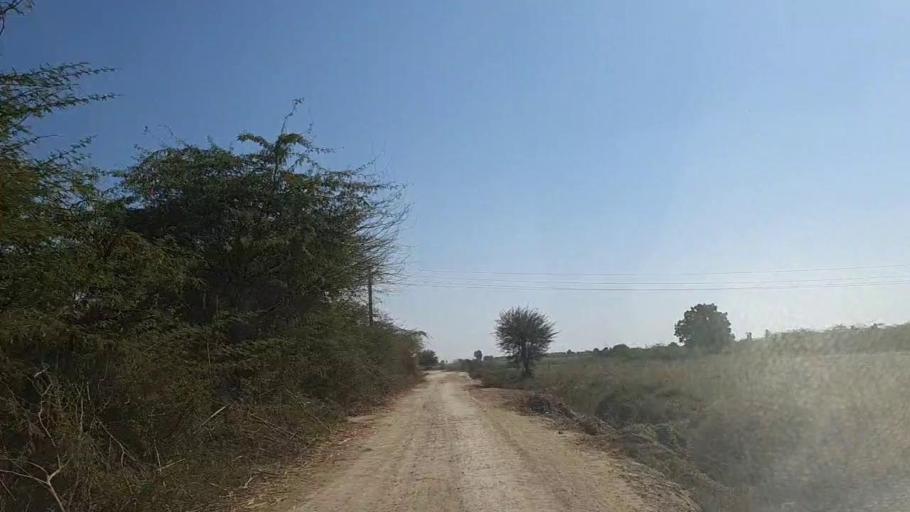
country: PK
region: Sindh
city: Naukot
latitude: 25.0366
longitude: 69.3915
